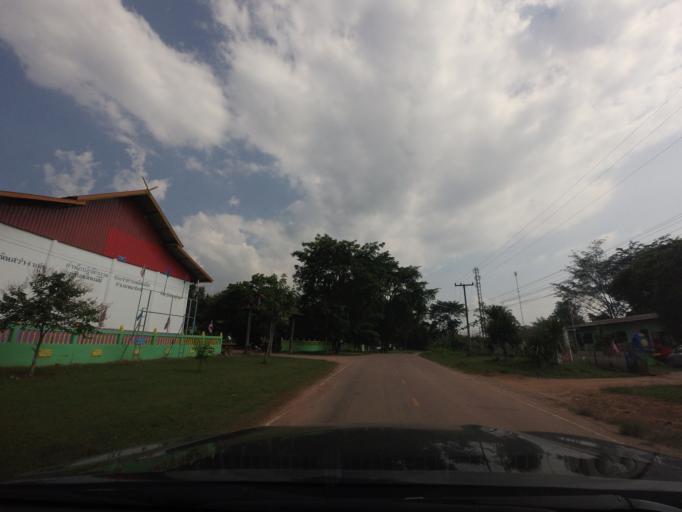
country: TH
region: Phitsanulok
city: Nakhon Thai
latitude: 17.0494
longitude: 100.9094
